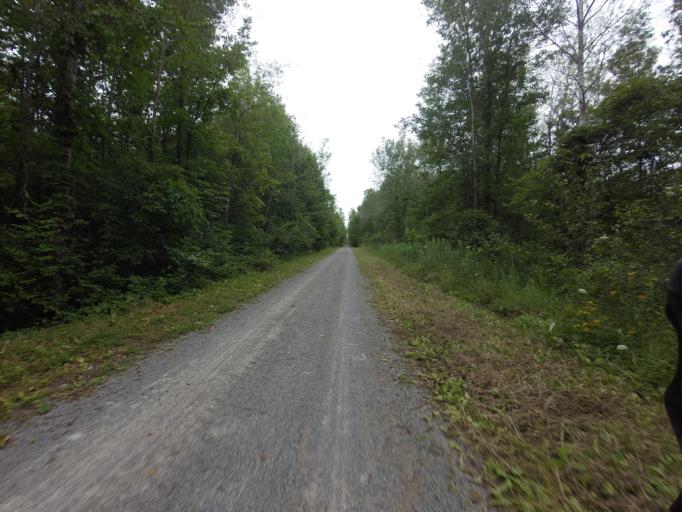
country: CA
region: Ontario
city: Ottawa
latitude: 45.2171
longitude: -75.6232
